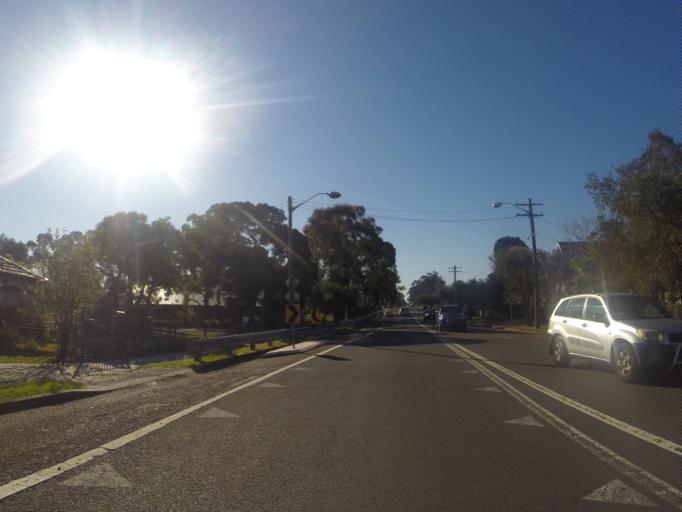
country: AU
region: New South Wales
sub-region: Bankstown
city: Regents Park
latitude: -33.8966
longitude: 151.0211
